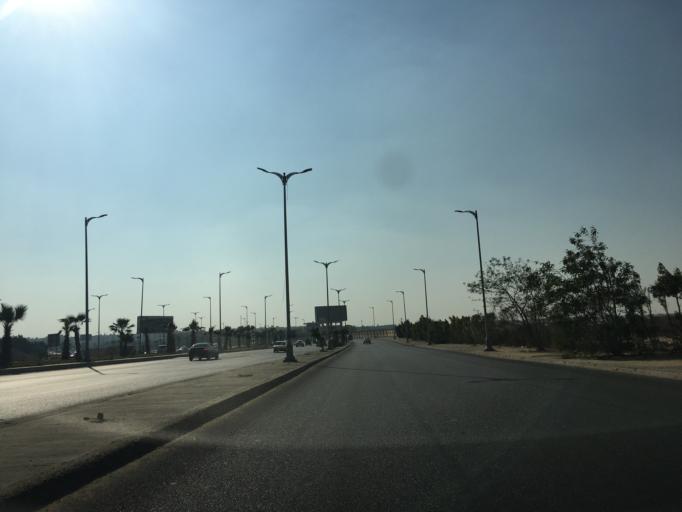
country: EG
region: Al Jizah
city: Madinat Sittah Uktubar
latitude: 29.9909
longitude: 30.9540
